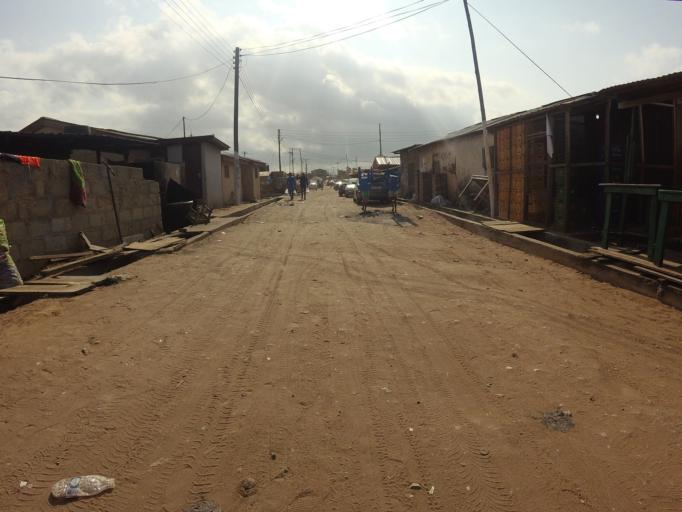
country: GH
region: Greater Accra
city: Dome
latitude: 5.6566
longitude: -0.2676
